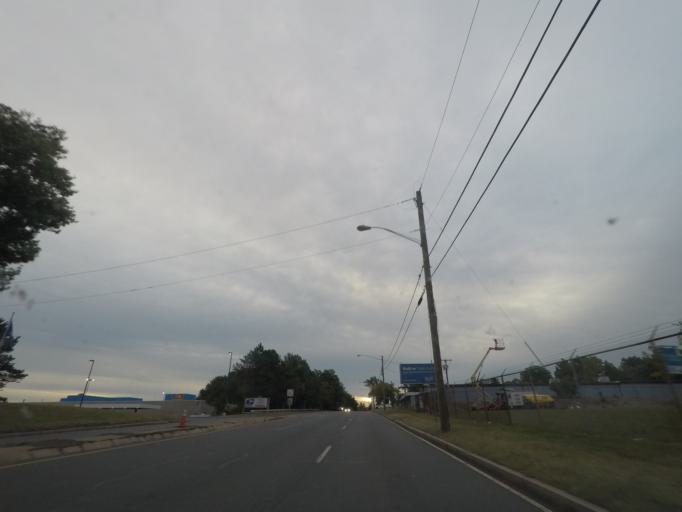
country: US
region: Massachusetts
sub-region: Hampden County
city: Ludlow
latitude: 42.1495
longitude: -72.5210
